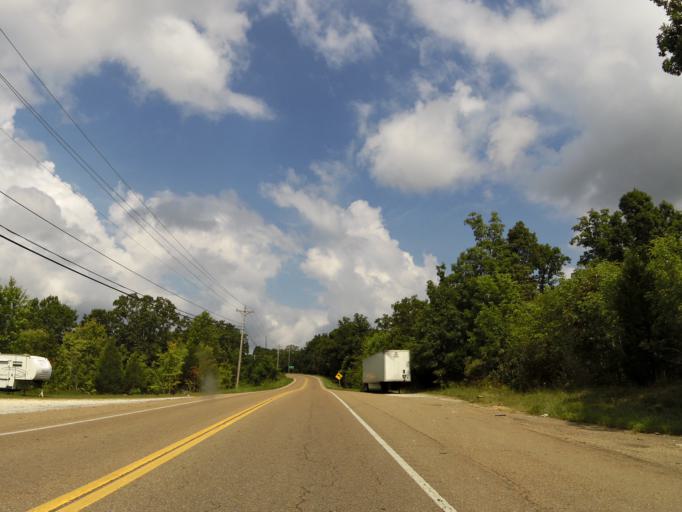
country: US
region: Tennessee
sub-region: Perry County
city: Linden
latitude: 35.6210
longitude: -87.8543
